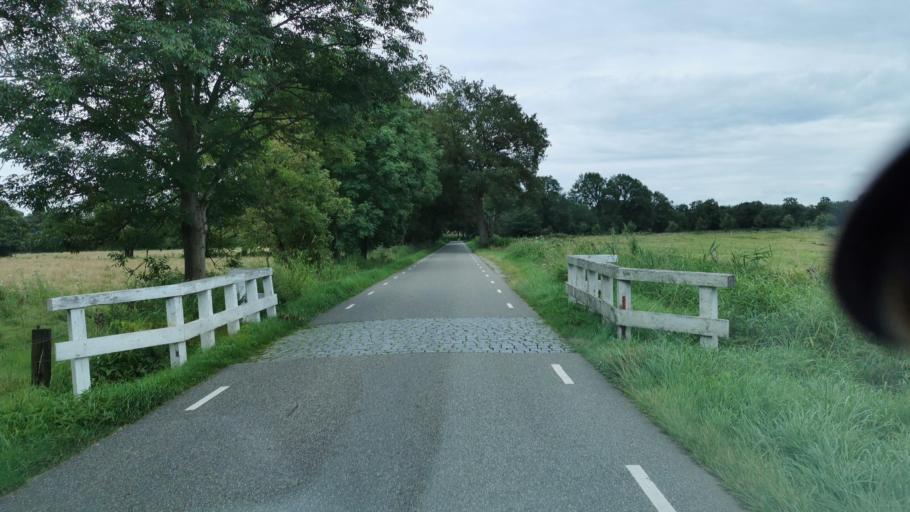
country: NL
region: Overijssel
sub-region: Gemeente Enschede
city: Enschede
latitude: 52.2395
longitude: 6.9497
